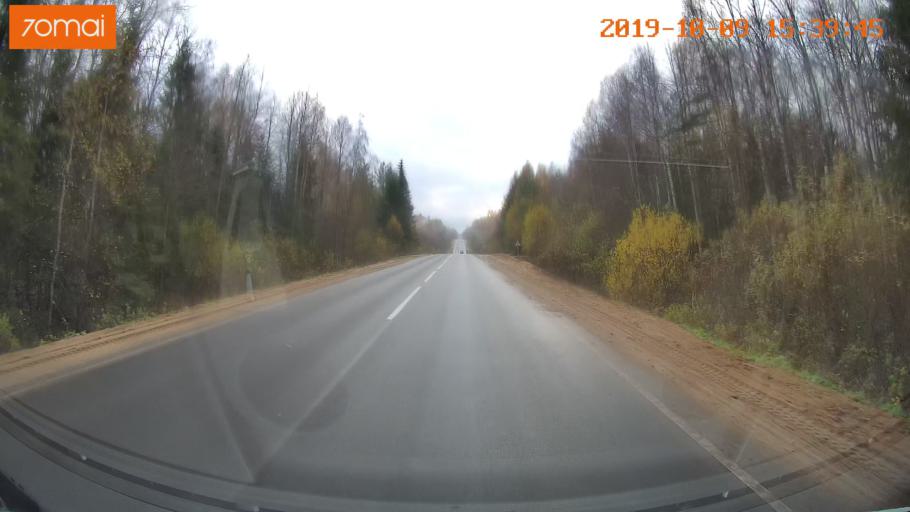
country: RU
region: Kostroma
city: Oktyabr'skiy
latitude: 57.8940
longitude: 41.1581
